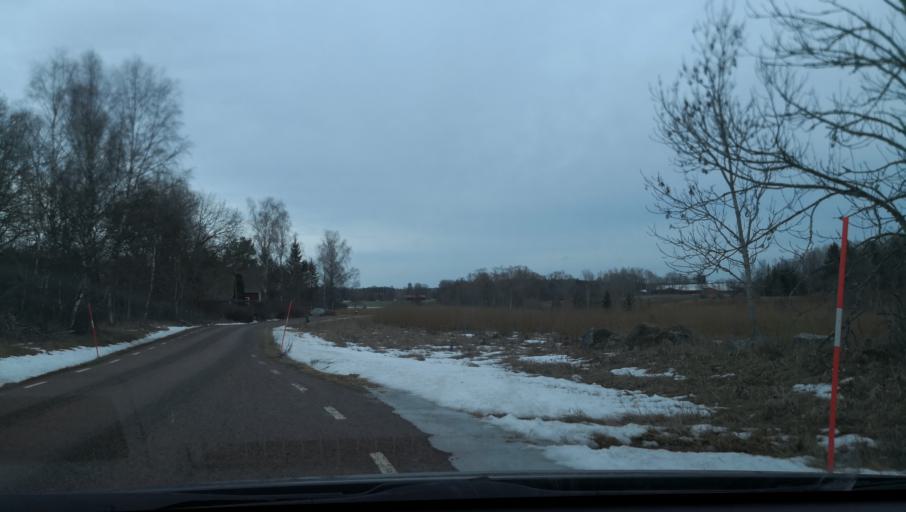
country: SE
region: Vaestmanland
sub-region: Vasteras
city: Skultuna
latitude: 59.6137
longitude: 16.4091
